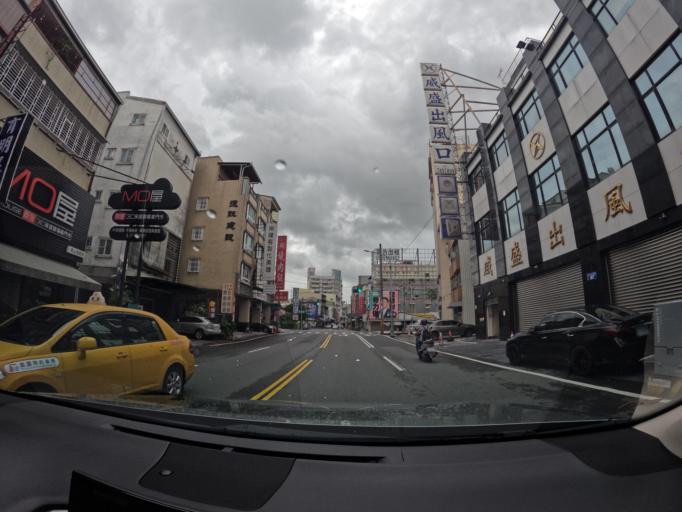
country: TW
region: Taiwan
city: Fengshan
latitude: 22.6266
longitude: 120.3532
